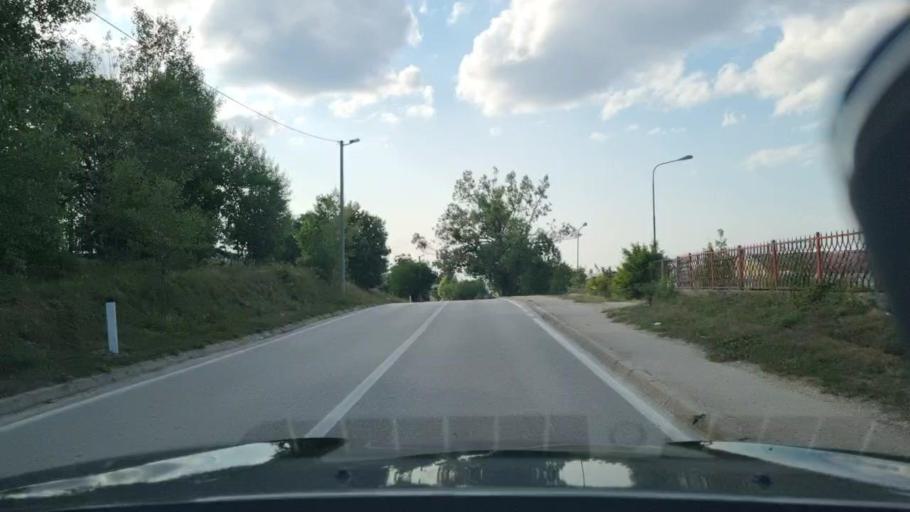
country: BA
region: Federation of Bosnia and Herzegovina
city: Glamoc
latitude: 44.0515
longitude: 16.8354
